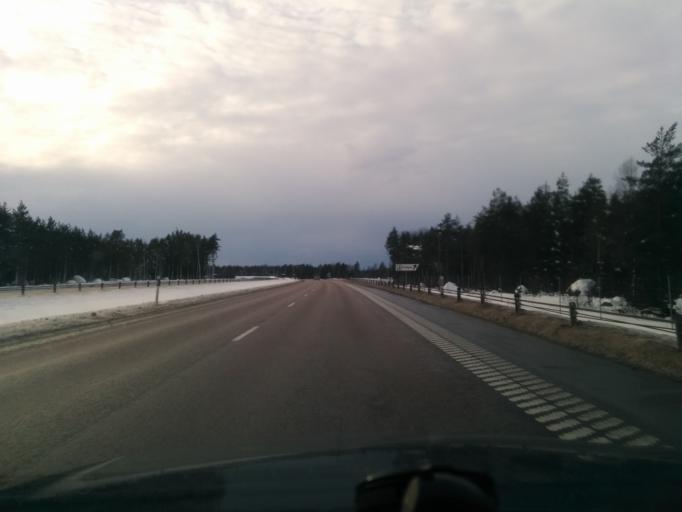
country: SE
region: Uppsala
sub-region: Enkopings Kommun
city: Hummelsta
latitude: 59.6409
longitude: 16.8912
